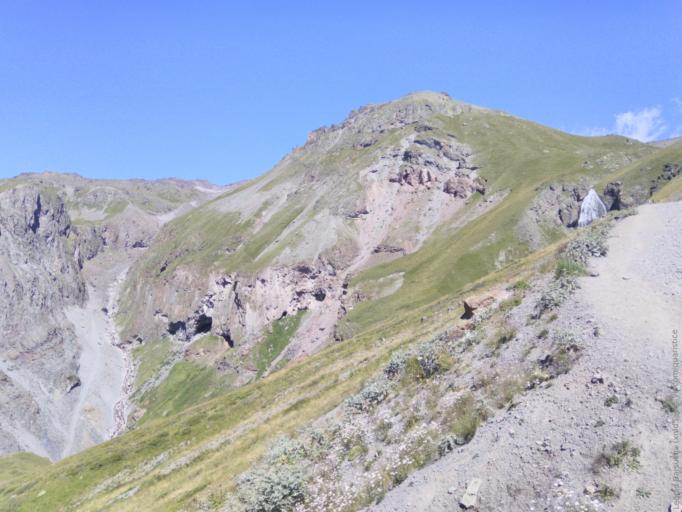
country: RU
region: Kabardino-Balkariya
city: Terskol
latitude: 43.2698
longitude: 42.4925
